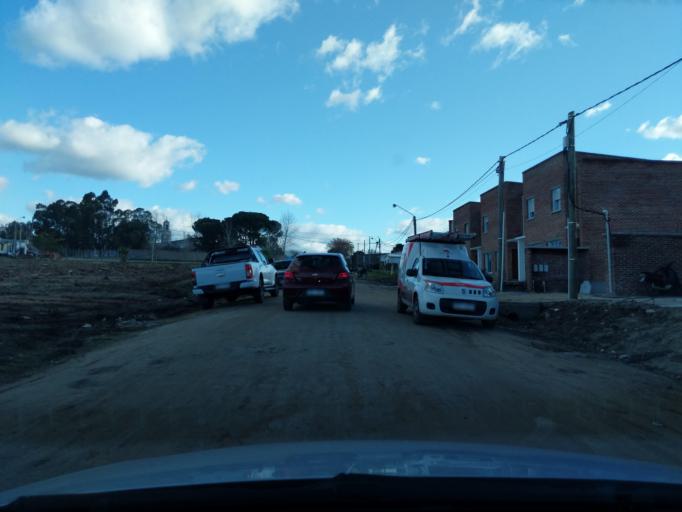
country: UY
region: Florida
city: Florida
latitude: -34.0961
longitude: -56.2263
